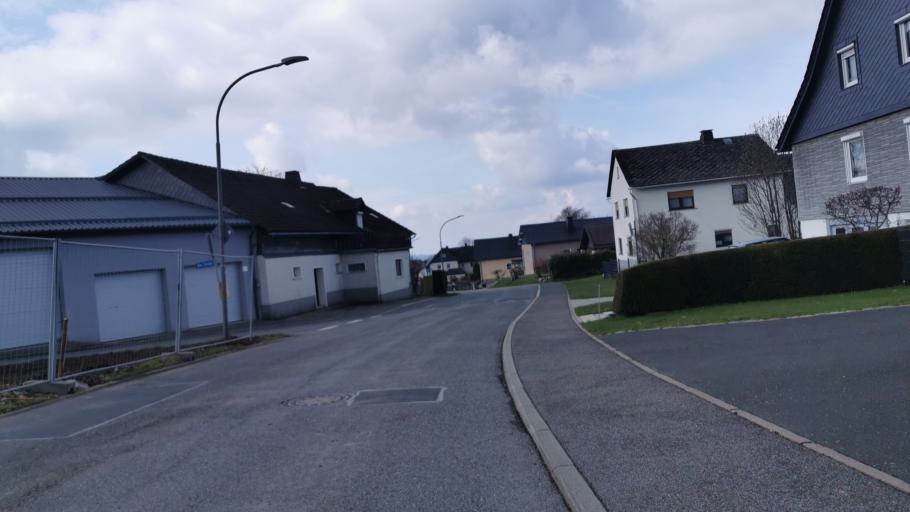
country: DE
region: Bavaria
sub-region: Upper Franconia
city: Tettau
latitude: 50.4482
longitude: 11.3193
